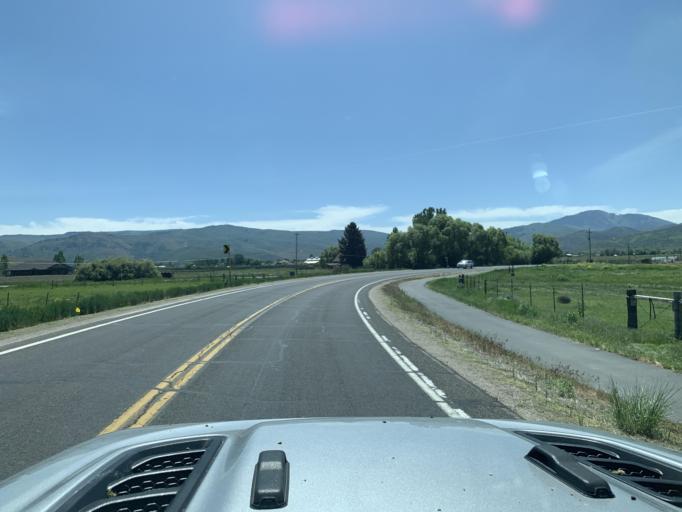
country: US
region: Utah
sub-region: Weber County
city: Wolf Creek
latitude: 41.2676
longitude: -111.7628
